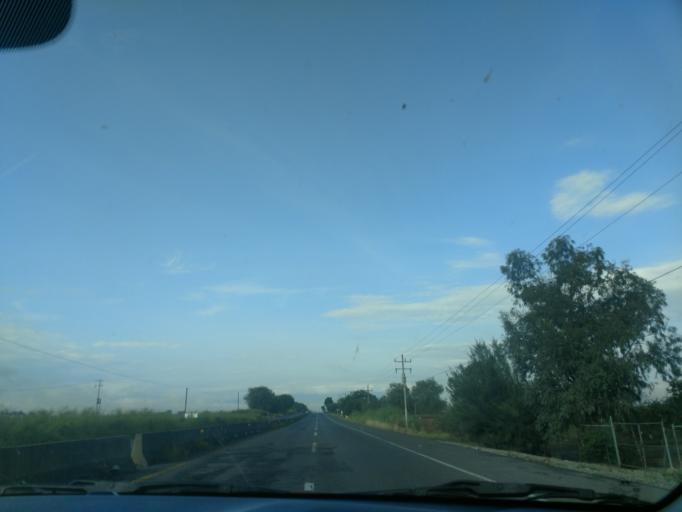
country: MX
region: Jalisco
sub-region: Ameca
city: Los Pocitos
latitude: 20.5493
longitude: -103.9015
